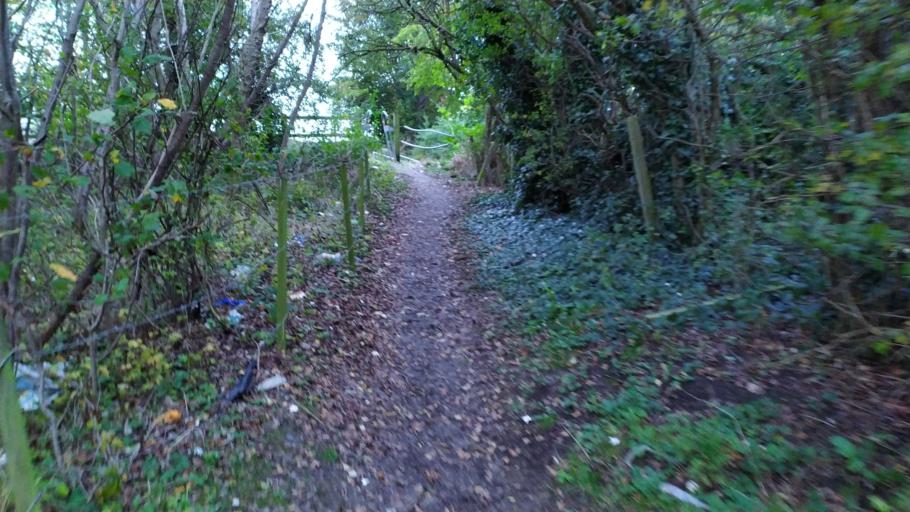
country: GB
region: England
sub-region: City and Borough of Leeds
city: Chapel Allerton
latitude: 53.8248
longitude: -1.5564
